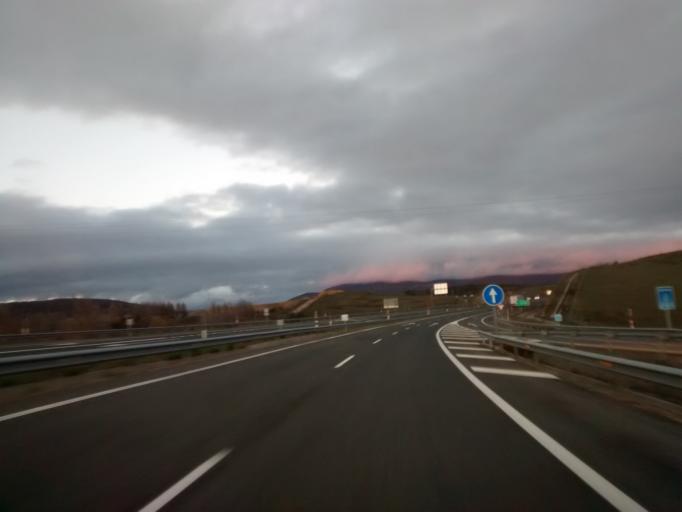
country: ES
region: Cantabria
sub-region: Provincia de Cantabria
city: Mataporquera
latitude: 42.8697
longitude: -4.1510
